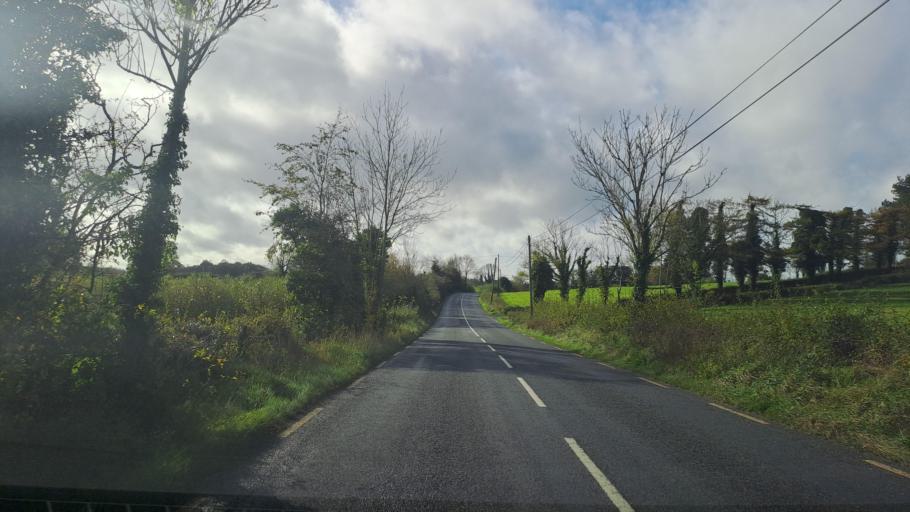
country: IE
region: Ulster
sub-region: An Cabhan
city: Cootehill
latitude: 54.1048
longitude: -6.9787
